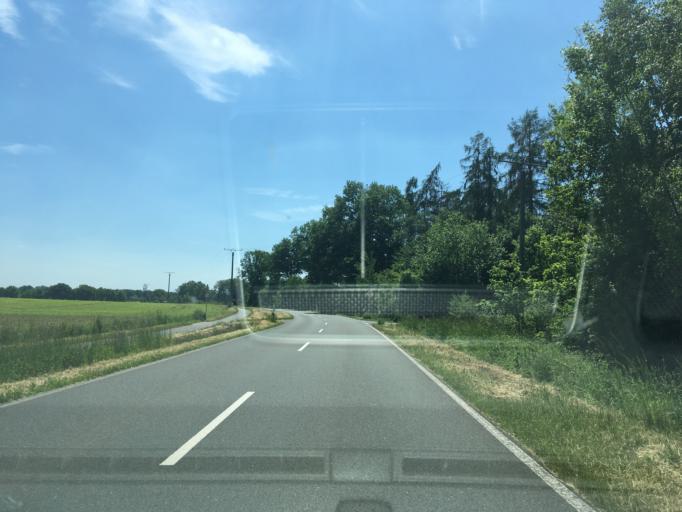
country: DE
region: North Rhine-Westphalia
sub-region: Regierungsbezirk Munster
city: Borken
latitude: 51.8756
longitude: 6.8282
